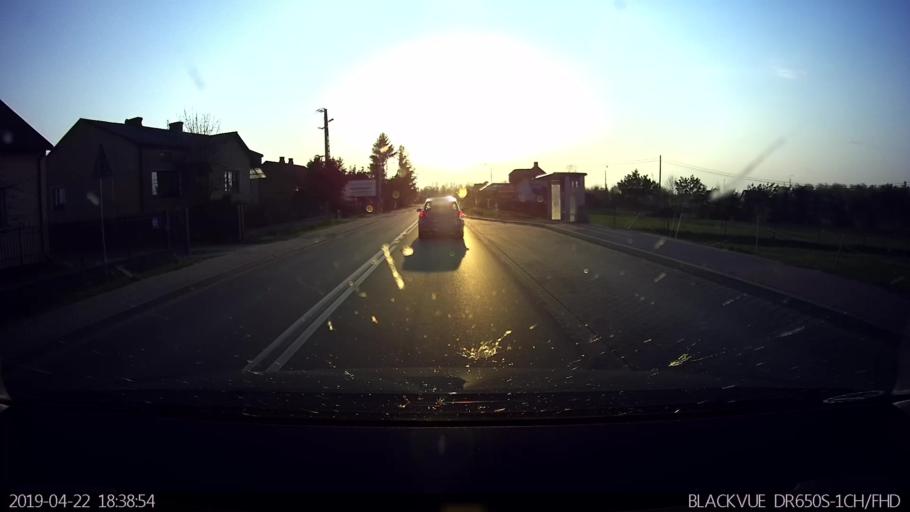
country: PL
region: Masovian Voivodeship
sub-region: Powiat wolominski
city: Dabrowka
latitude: 52.4414
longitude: 21.2915
